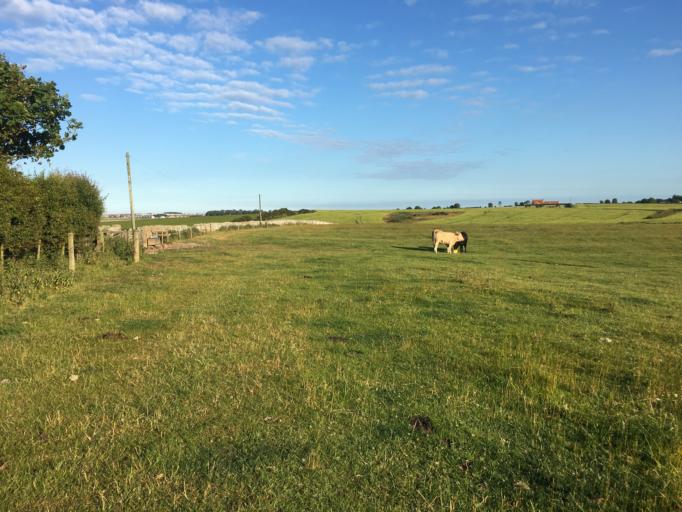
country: GB
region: England
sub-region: Northumberland
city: Bamburgh
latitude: 55.5979
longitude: -1.6951
